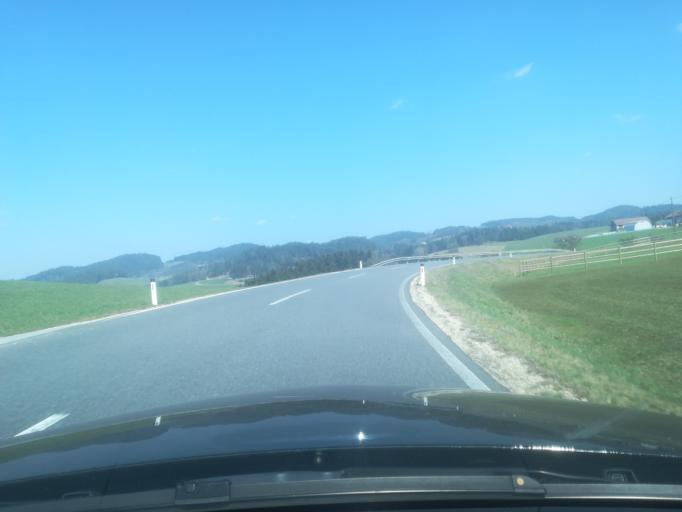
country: AT
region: Upper Austria
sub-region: Politischer Bezirk Perg
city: Perg
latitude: 48.3704
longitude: 14.6822
